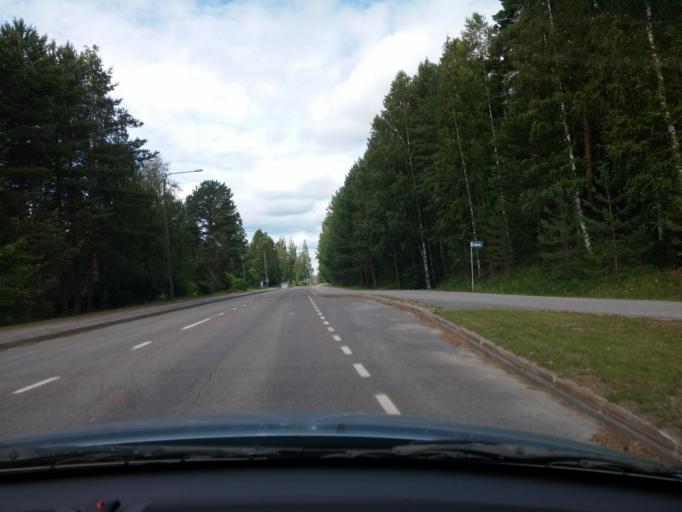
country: FI
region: Central Finland
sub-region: Saarijaervi-Viitasaari
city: Saarijaervi
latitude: 62.7095
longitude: 25.2177
